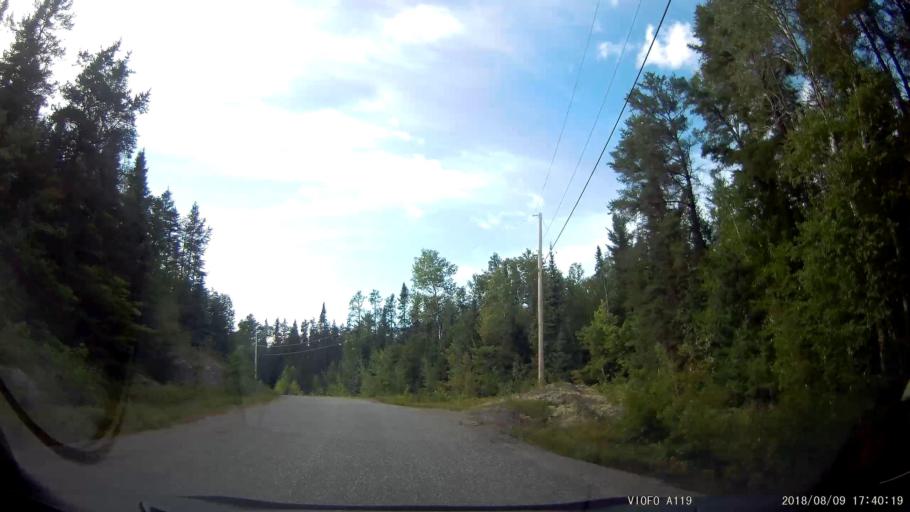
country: CA
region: Ontario
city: Rayside-Balfour
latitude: 46.6070
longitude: -81.5007
